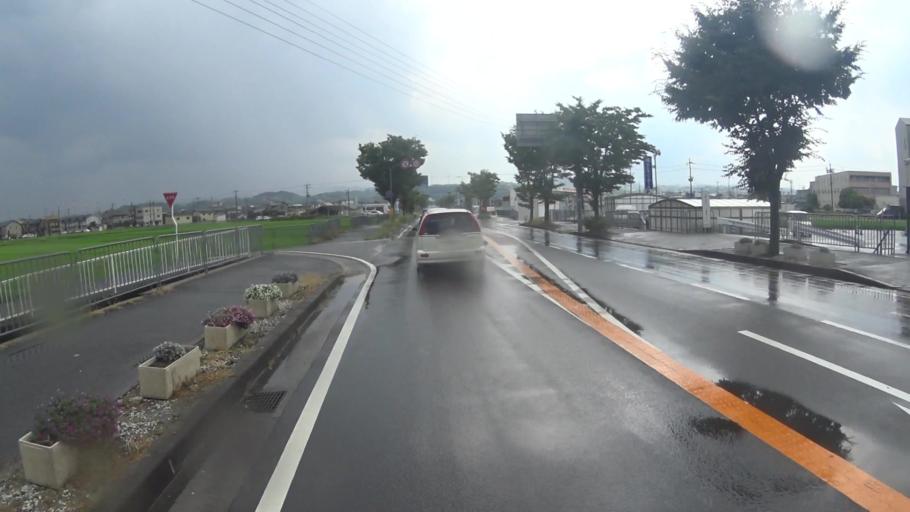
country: JP
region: Kyoto
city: Tanabe
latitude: 34.8181
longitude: 135.7879
